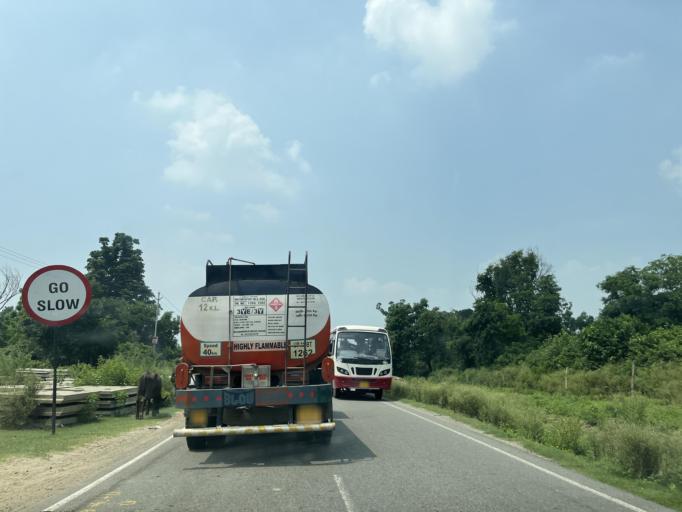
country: IN
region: Uttarakhand
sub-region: Haridwar
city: Haridwar
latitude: 29.8443
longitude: 78.1885
